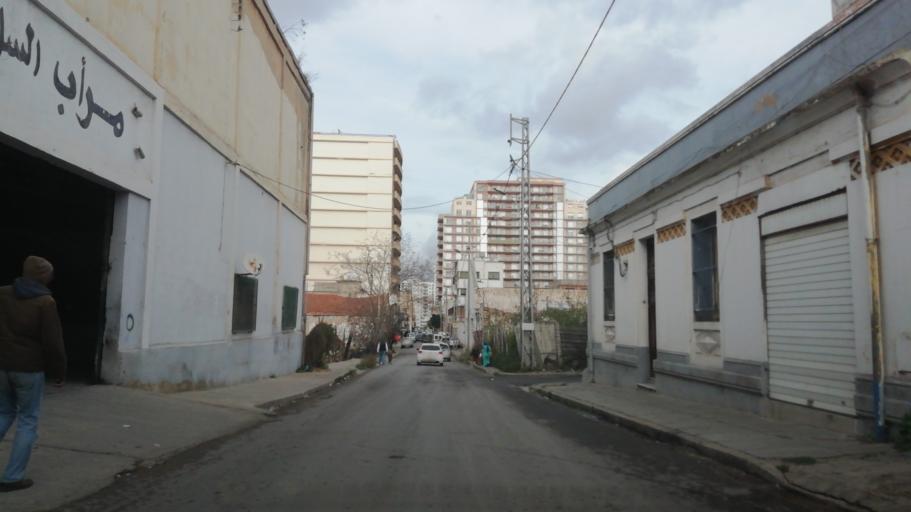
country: DZ
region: Oran
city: Oran
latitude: 35.7002
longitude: -0.6254
